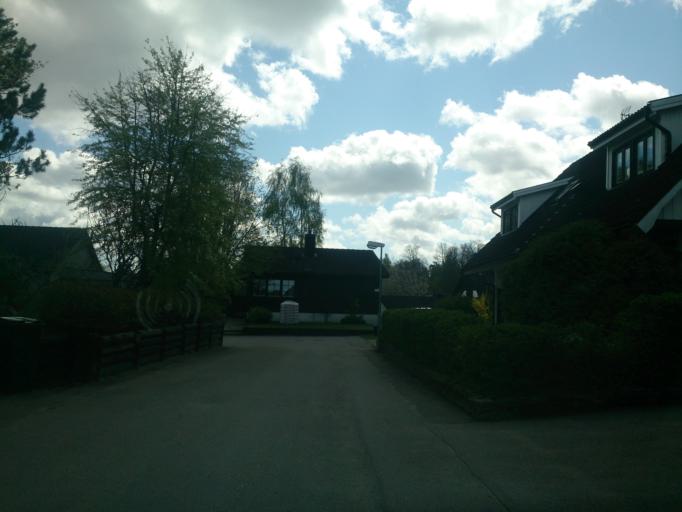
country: SE
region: OEstergoetland
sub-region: Atvidabergs Kommun
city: Atvidaberg
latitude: 58.2017
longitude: 15.9756
